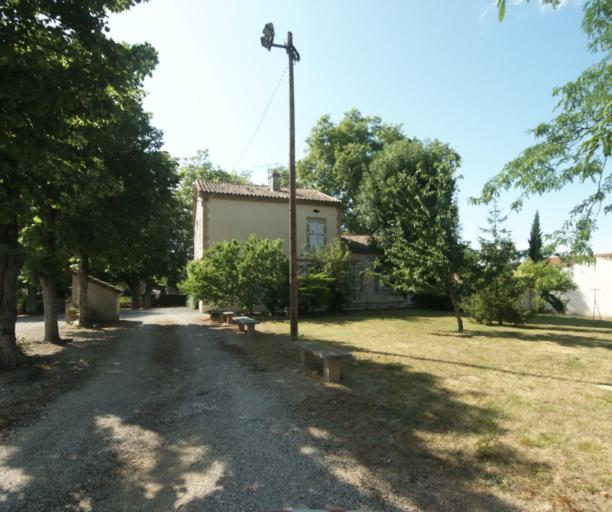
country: FR
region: Midi-Pyrenees
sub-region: Departement du Tarn
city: Puylaurens
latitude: 43.5211
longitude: 1.9857
